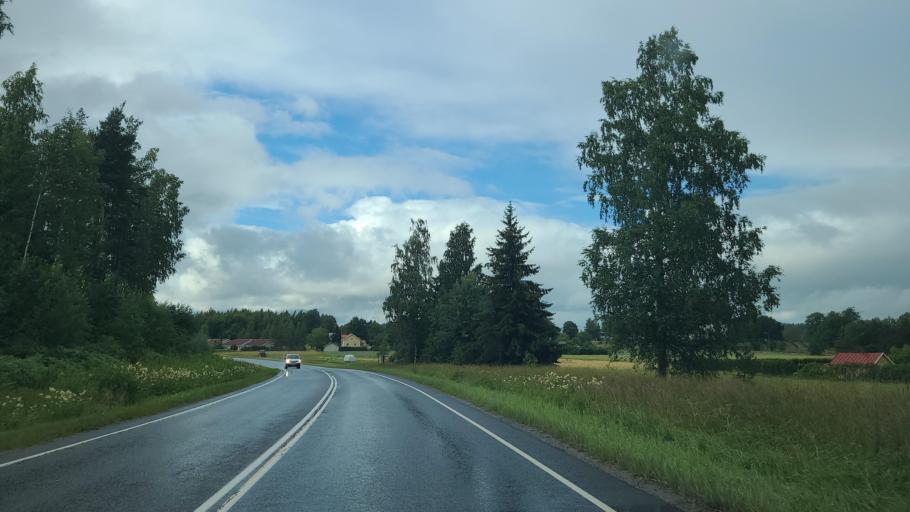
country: FI
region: Varsinais-Suomi
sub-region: Turku
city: Sauvo
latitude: 60.3387
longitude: 22.7011
